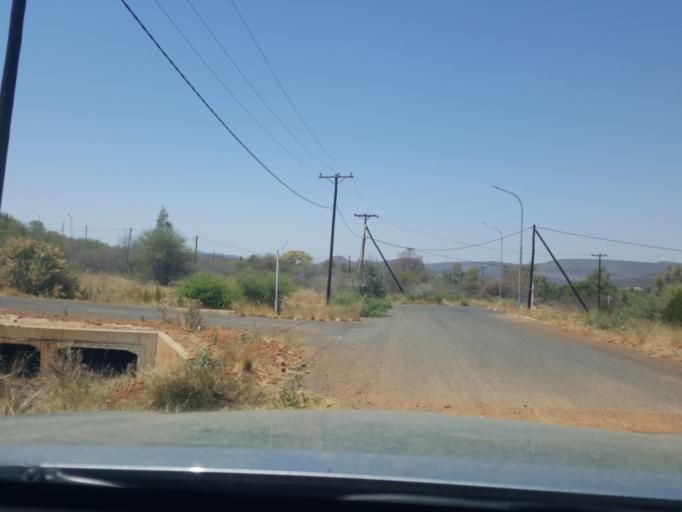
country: BW
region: South East
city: Lobatse
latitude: -25.1902
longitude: 25.6749
